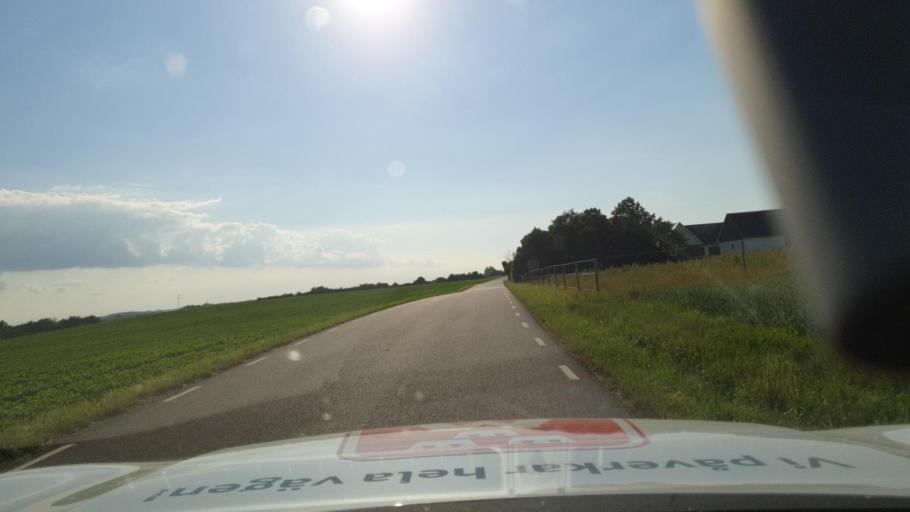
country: SE
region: Skane
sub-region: Skurups Kommun
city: Rydsgard
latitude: 55.5033
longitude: 13.5756
